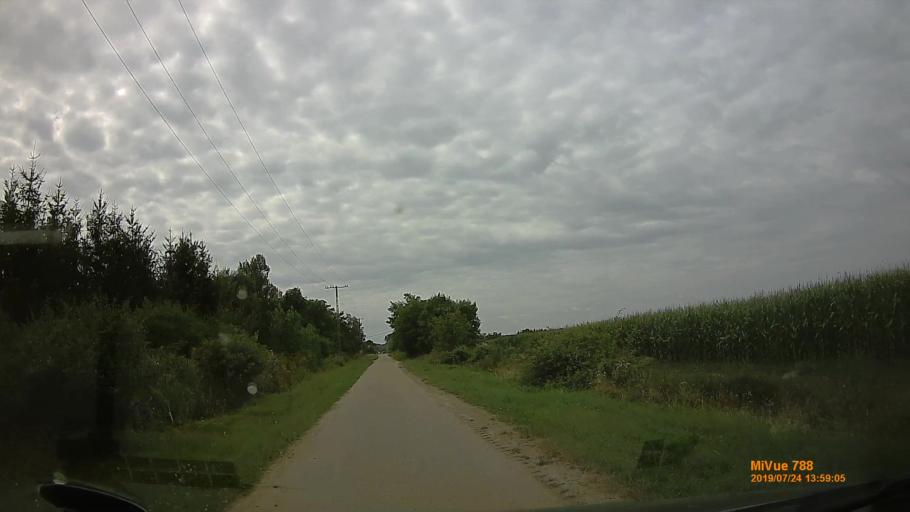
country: HU
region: Szabolcs-Szatmar-Bereg
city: Aranyosapati
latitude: 48.2586
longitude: 22.3174
